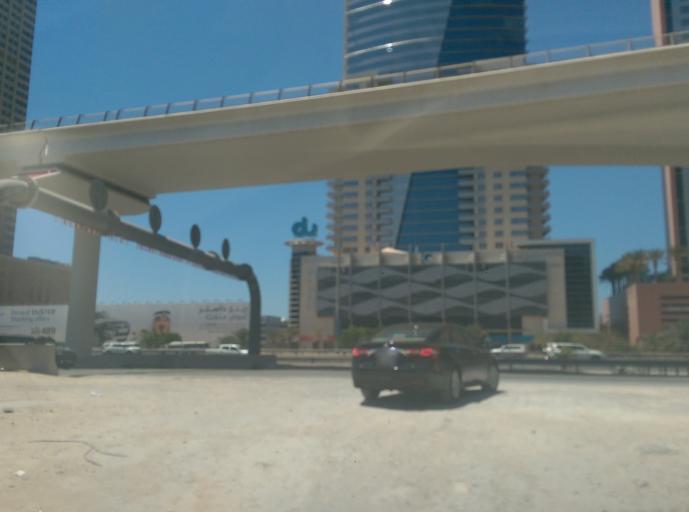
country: AE
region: Dubai
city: Dubai
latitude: 25.1007
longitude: 55.1725
